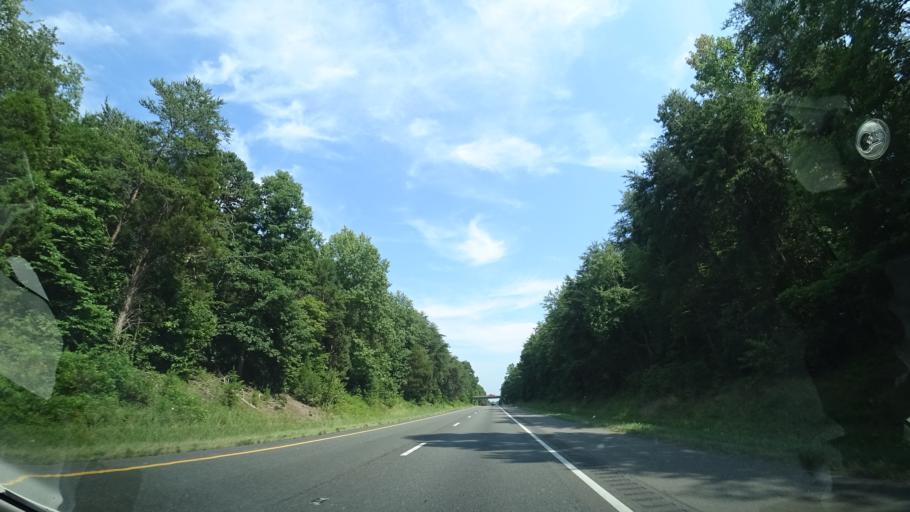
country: US
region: Virginia
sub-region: Goochland County
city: Goochland
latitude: 37.7830
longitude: -77.8909
